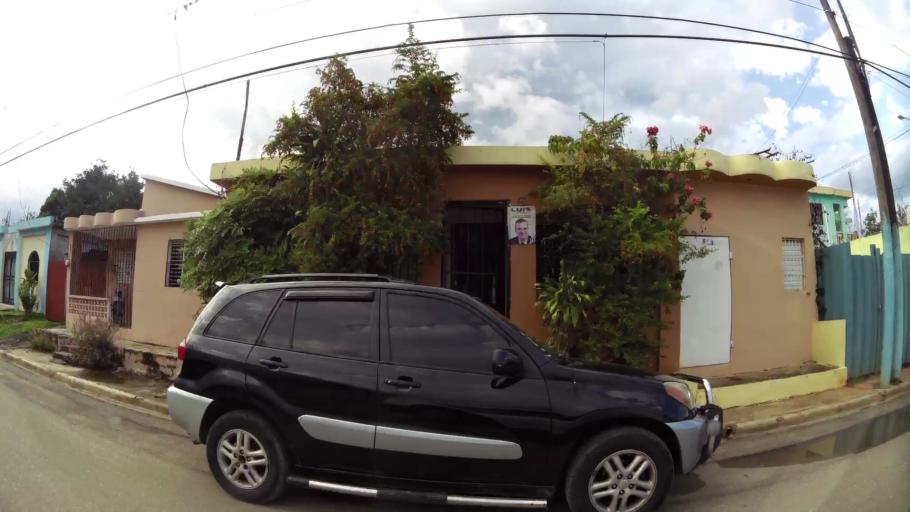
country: DO
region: San Cristobal
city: Villa Altagracia
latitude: 18.6723
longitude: -70.1707
